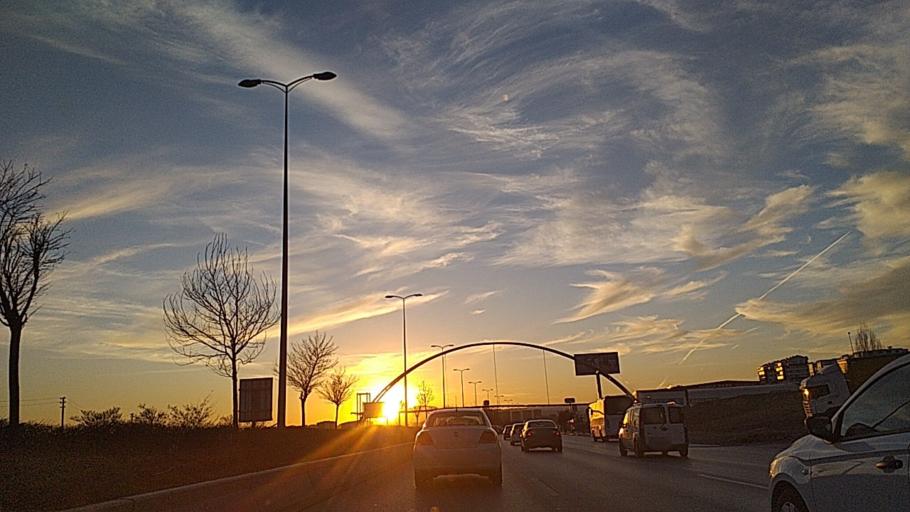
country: TR
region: Ankara
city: Etimesgut
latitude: 39.9628
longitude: 32.6593
